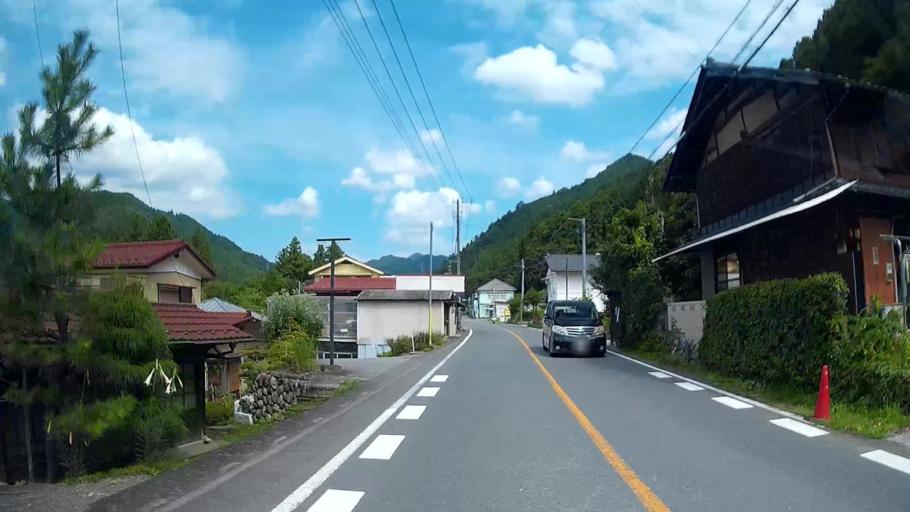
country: JP
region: Tokyo
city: Ome
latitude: 35.8827
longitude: 139.1838
